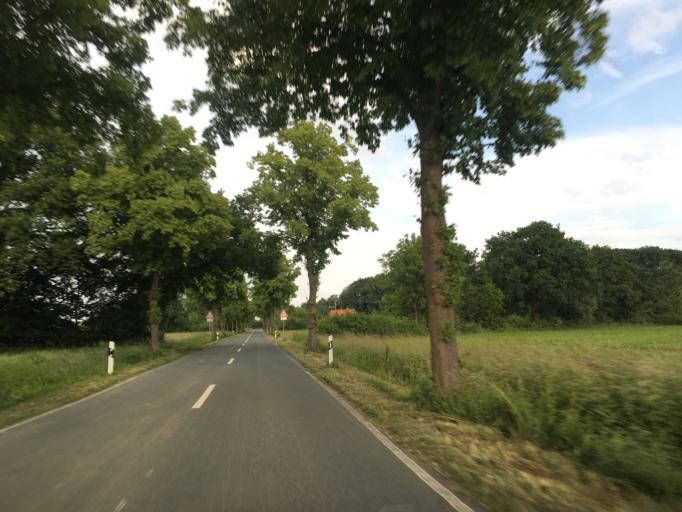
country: DE
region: North Rhine-Westphalia
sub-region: Regierungsbezirk Munster
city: Altenberge
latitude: 51.9911
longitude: 7.4904
